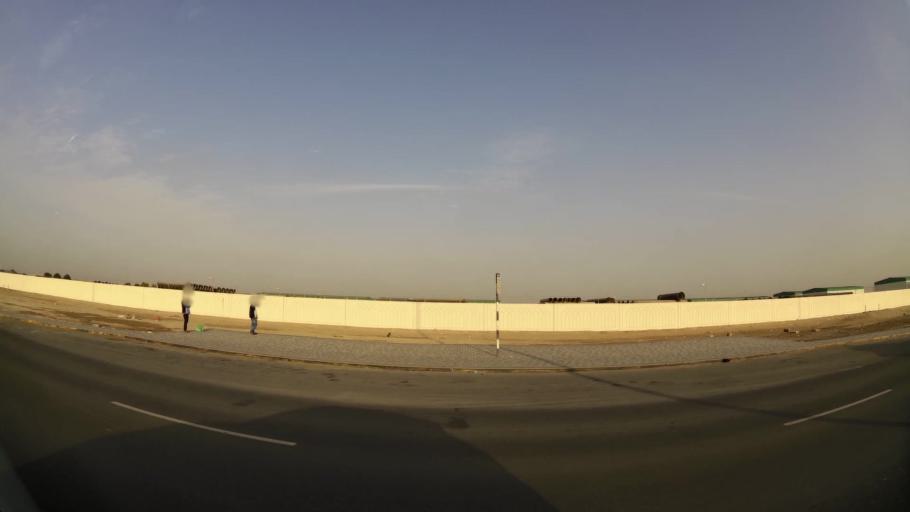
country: AE
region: Abu Dhabi
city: Abu Dhabi
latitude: 24.3526
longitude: 54.5022
